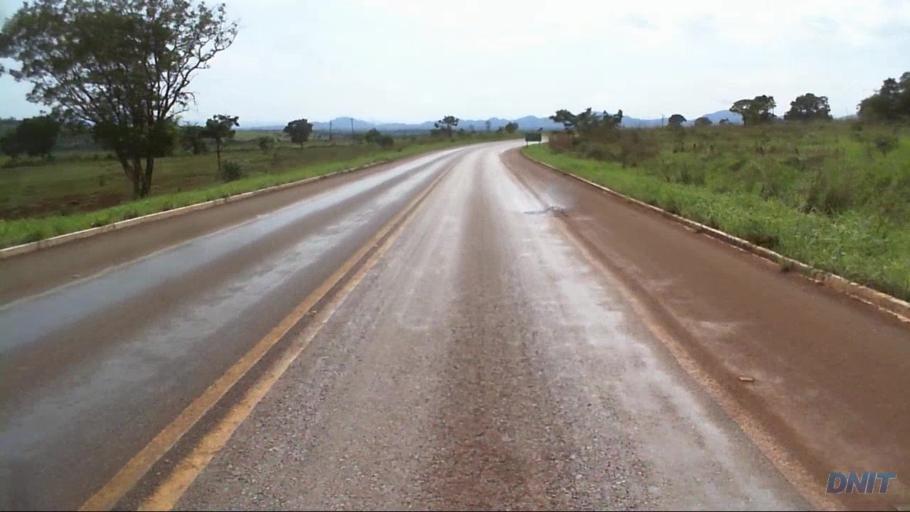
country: BR
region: Goias
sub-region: Barro Alto
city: Barro Alto
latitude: -14.9879
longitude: -48.9122
